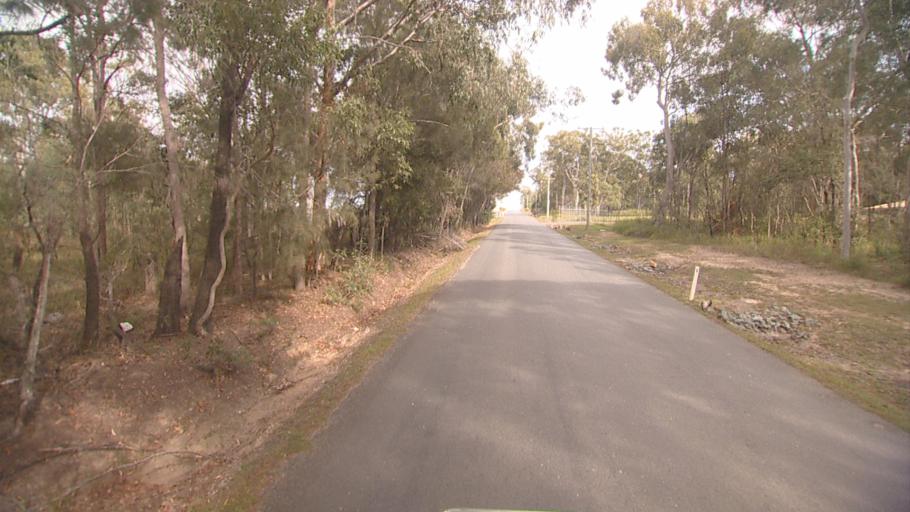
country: AU
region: Queensland
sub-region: Logan
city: Woodridge
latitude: -27.6534
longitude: 153.0850
